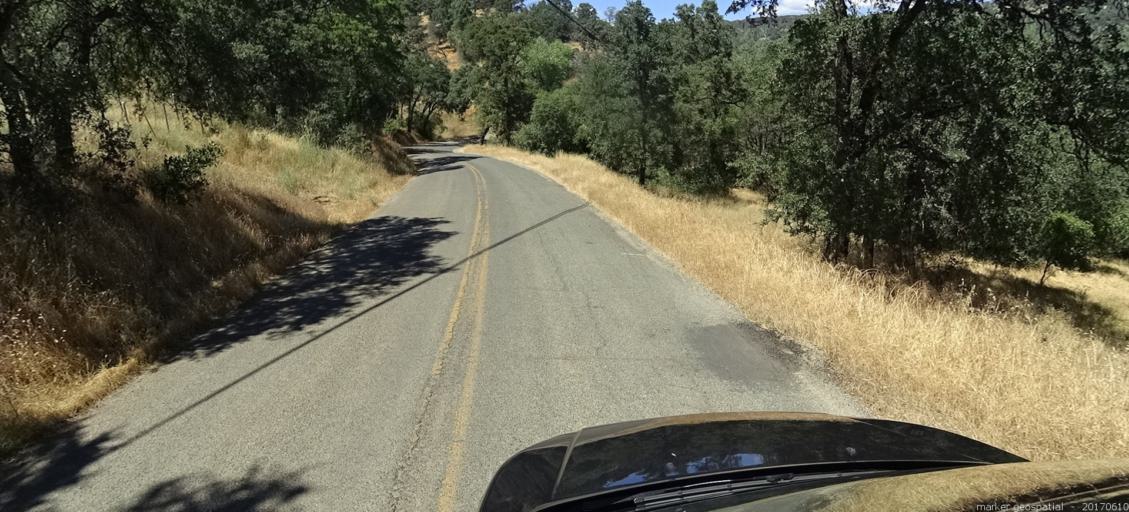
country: US
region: California
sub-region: Butte County
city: Oroville
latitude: 39.5490
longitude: -121.5410
